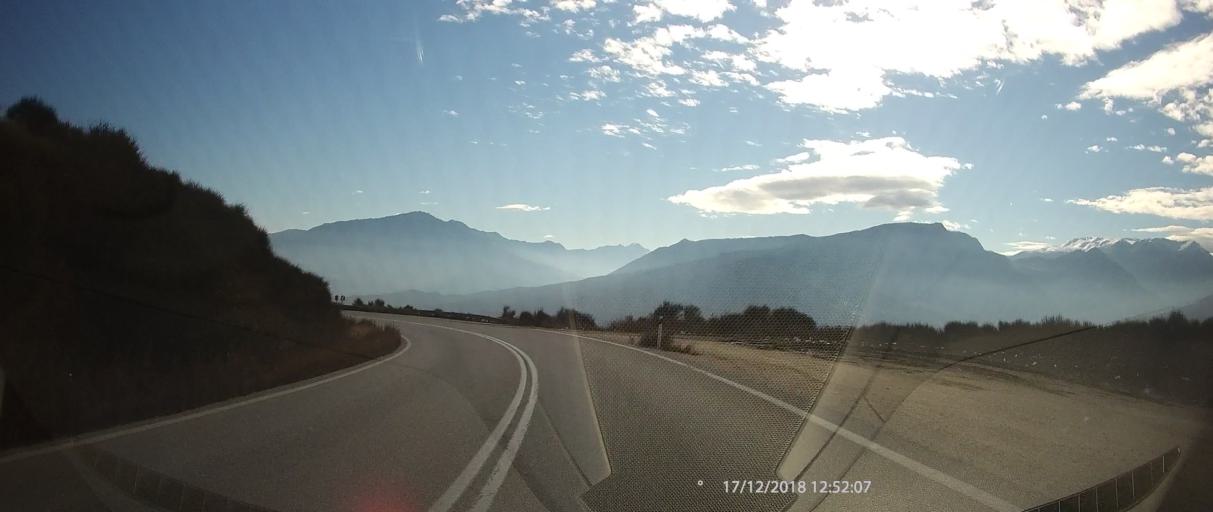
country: GR
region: Thessaly
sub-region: Trikala
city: Kastraki
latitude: 39.7592
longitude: 21.4740
